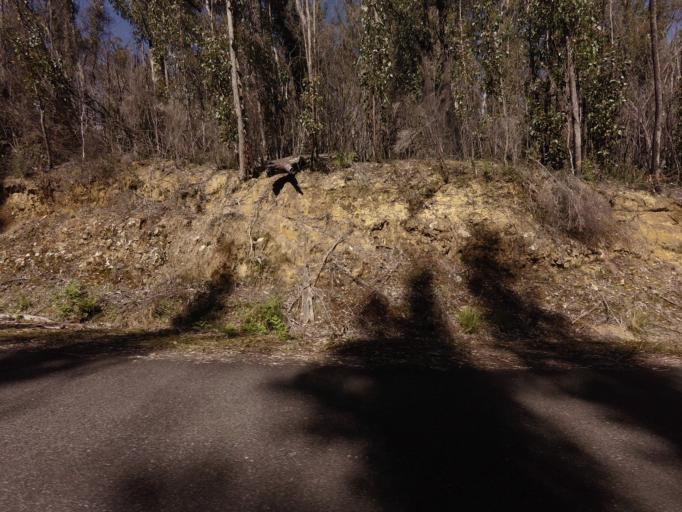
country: AU
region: Tasmania
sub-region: Huon Valley
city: Geeveston
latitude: -42.8415
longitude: 146.2536
